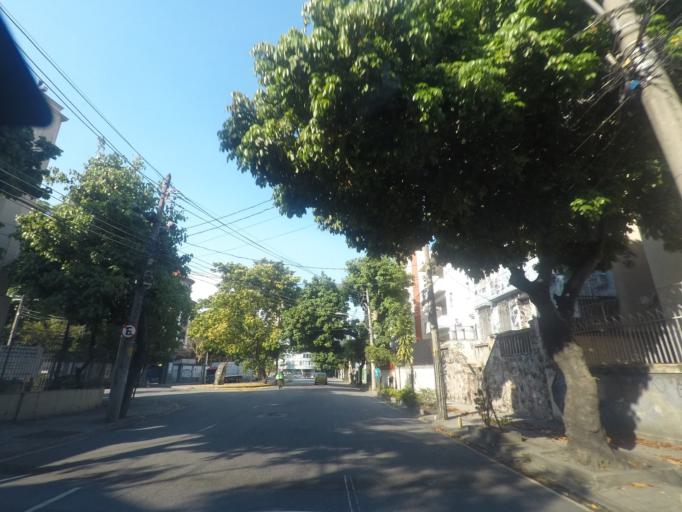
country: BR
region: Rio de Janeiro
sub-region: Rio De Janeiro
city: Rio de Janeiro
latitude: -22.9153
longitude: -43.2167
